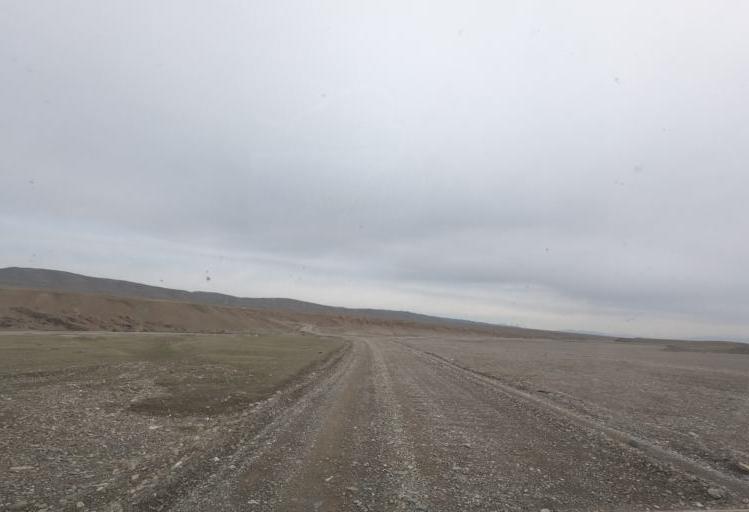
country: KG
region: Naryn
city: Baetov
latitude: 40.9338
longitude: 75.2786
